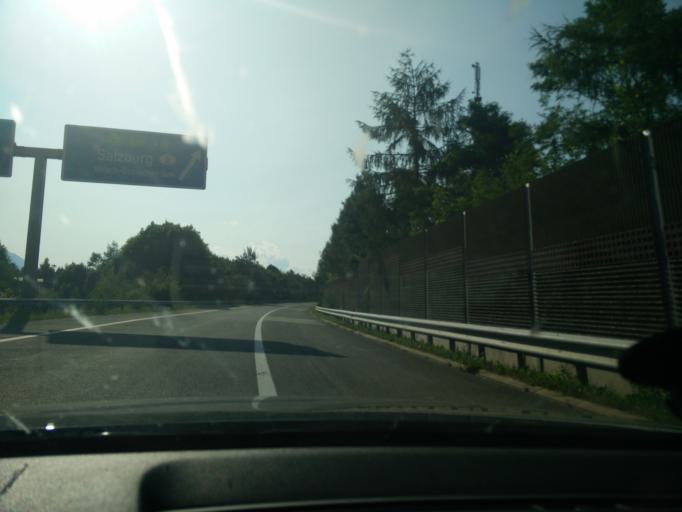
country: AT
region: Carinthia
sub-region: Politischer Bezirk Villach Land
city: Wernberg
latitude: 46.6206
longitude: 13.9050
